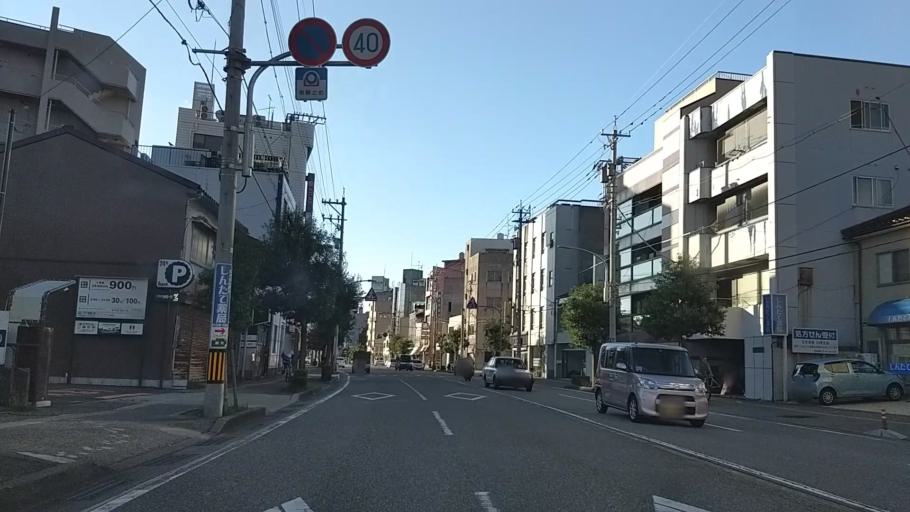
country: JP
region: Ishikawa
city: Nonoichi
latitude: 36.5562
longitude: 136.6572
